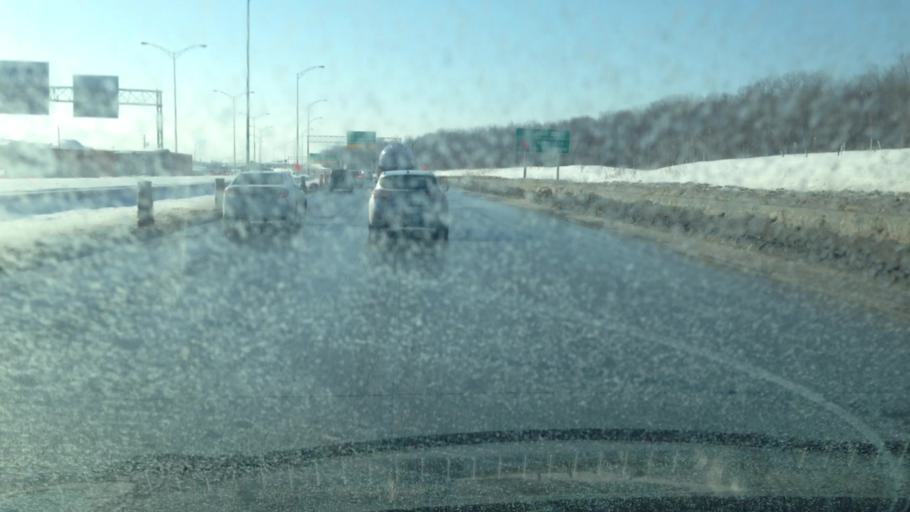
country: CA
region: Quebec
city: Saint-Raymond
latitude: 45.4604
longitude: -73.6179
